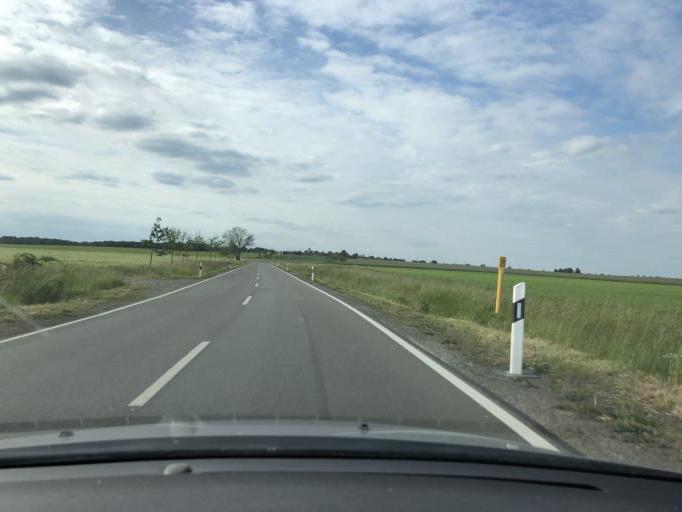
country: DE
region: Saxony
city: Brandis
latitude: 51.3045
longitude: 12.6509
